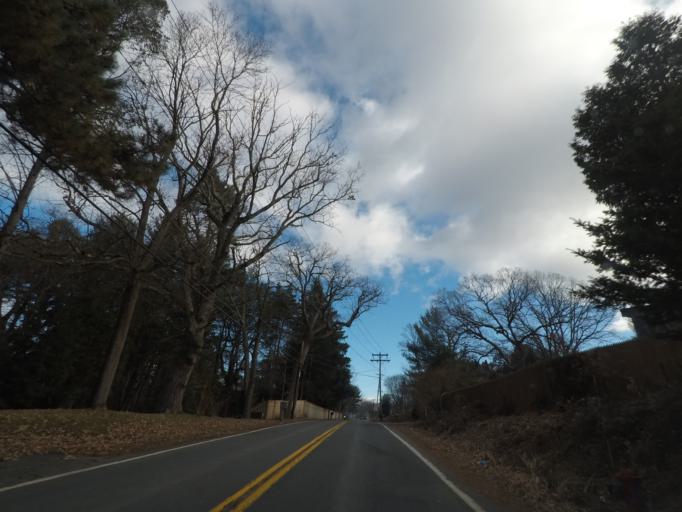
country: US
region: New York
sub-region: Saratoga County
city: Waterford
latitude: 42.7915
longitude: -73.6520
